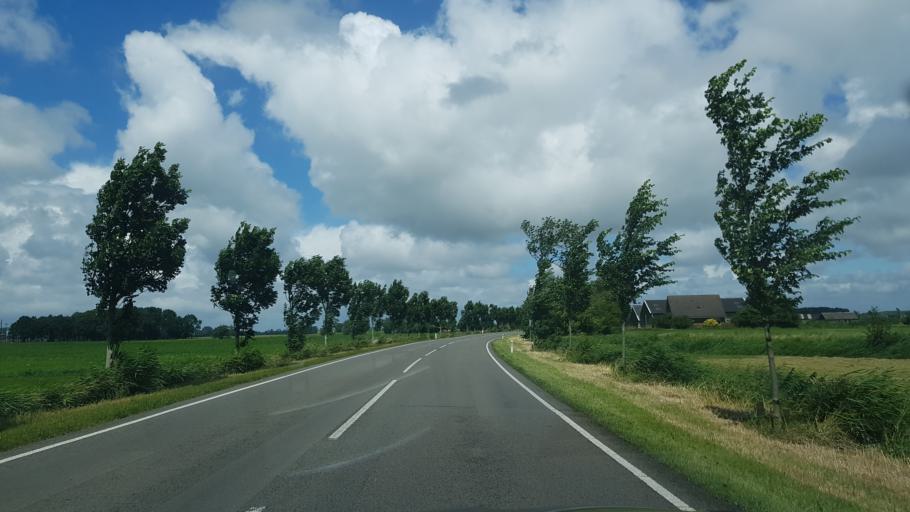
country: NL
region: Groningen
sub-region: Gemeente Winsum
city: Winsum
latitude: 53.3459
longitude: 6.5065
